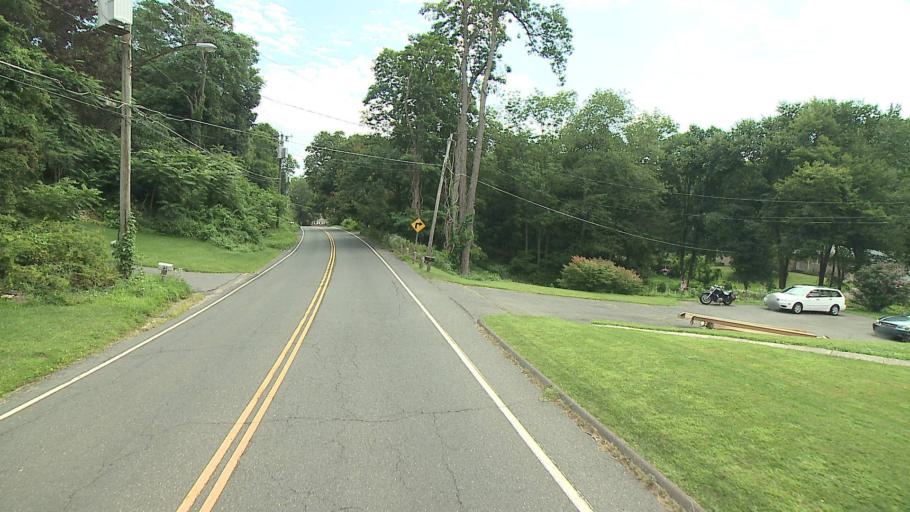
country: US
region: New York
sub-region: Putnam County
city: Putnam Lake
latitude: 41.4444
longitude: -73.5103
